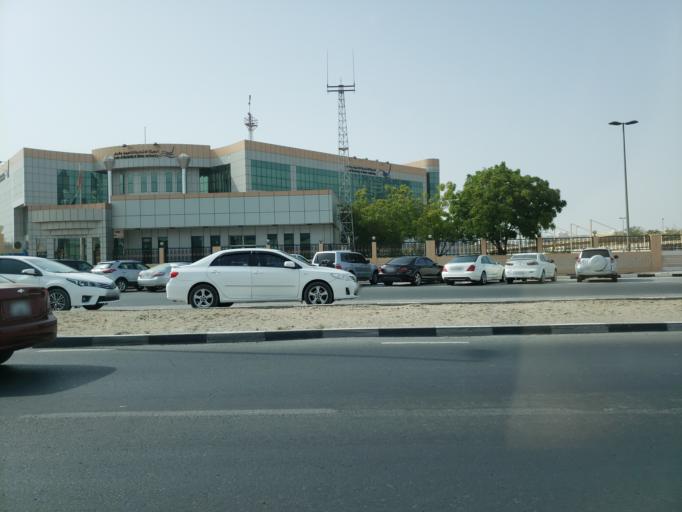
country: AE
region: Ajman
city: Ajman
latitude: 25.3925
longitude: 55.4769
